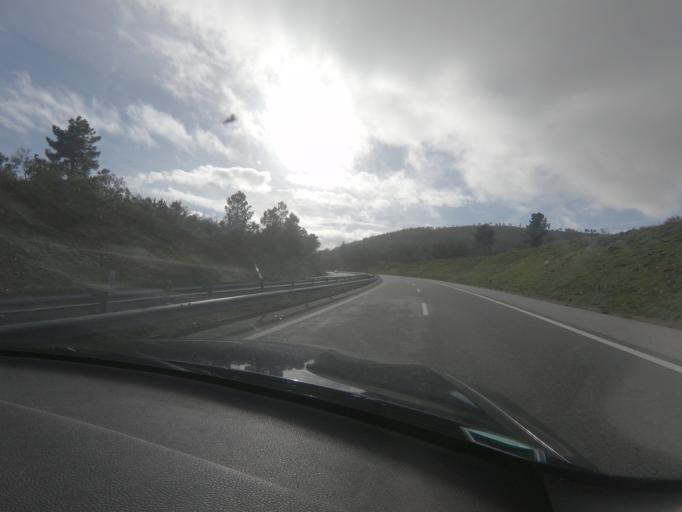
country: PT
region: Viseu
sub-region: Lamego
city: Lamego
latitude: 41.0554
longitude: -7.8395
